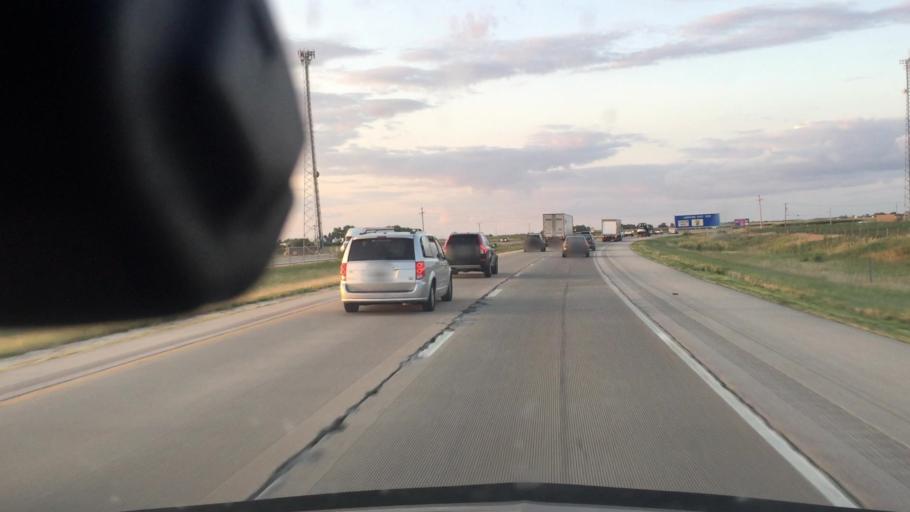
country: US
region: Illinois
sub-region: Livingston County
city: Dwight
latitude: 41.1069
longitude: -88.4475
